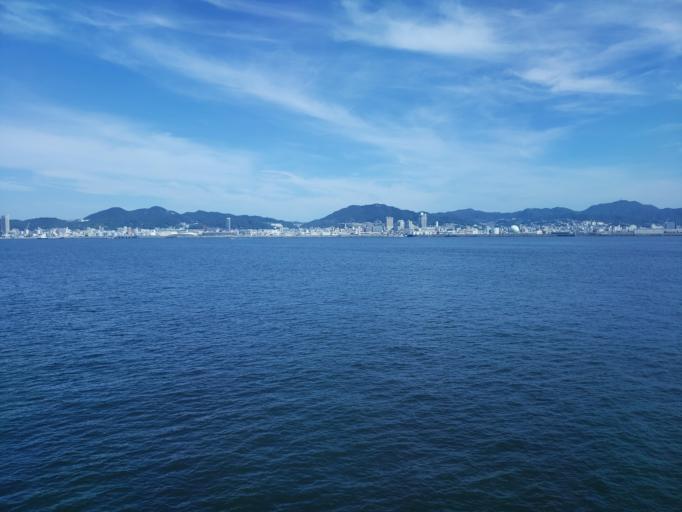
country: JP
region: Hyogo
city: Kobe
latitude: 34.6307
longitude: 135.1591
